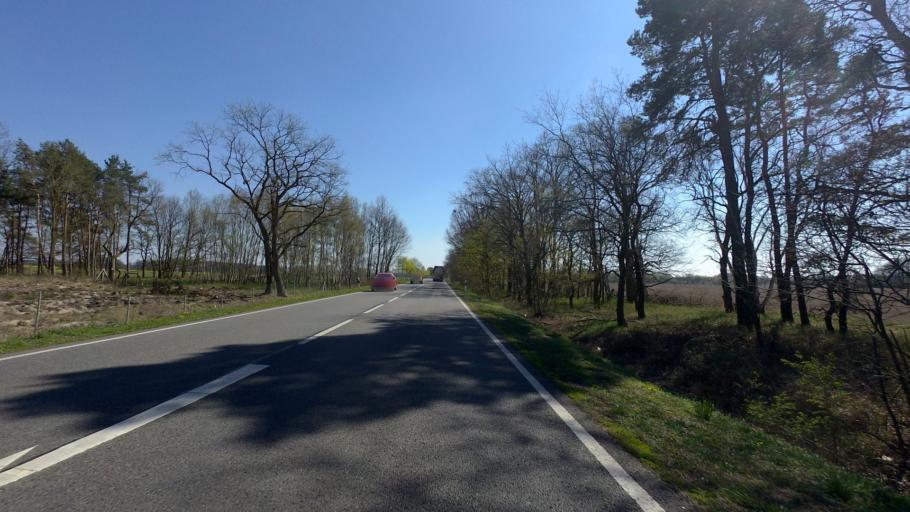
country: DE
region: Saxony-Anhalt
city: Pretzier
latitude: 52.7696
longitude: 11.2364
